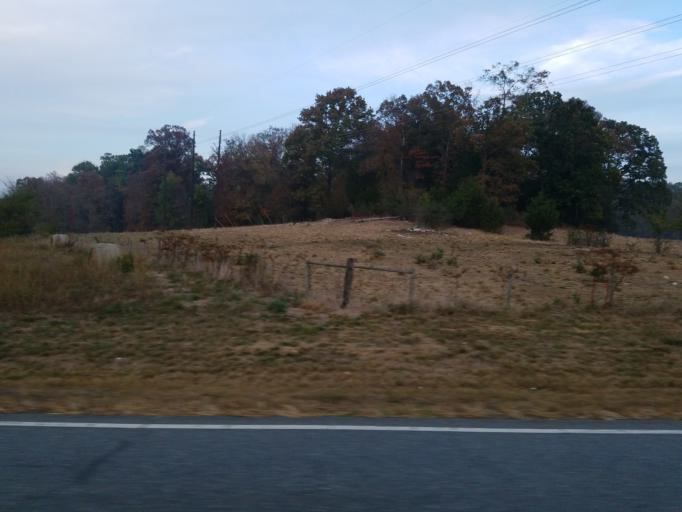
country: US
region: Georgia
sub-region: Murray County
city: Chatsworth
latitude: 34.5874
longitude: -84.7188
